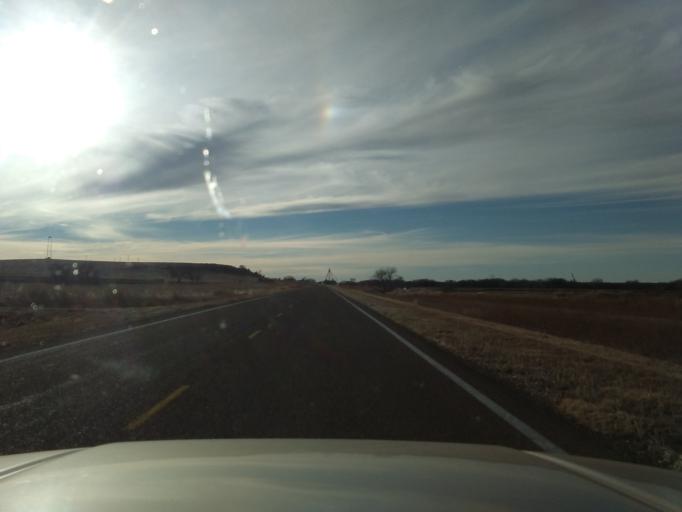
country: US
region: Kansas
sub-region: Norton County
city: Norton
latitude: 39.7432
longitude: -100.1641
